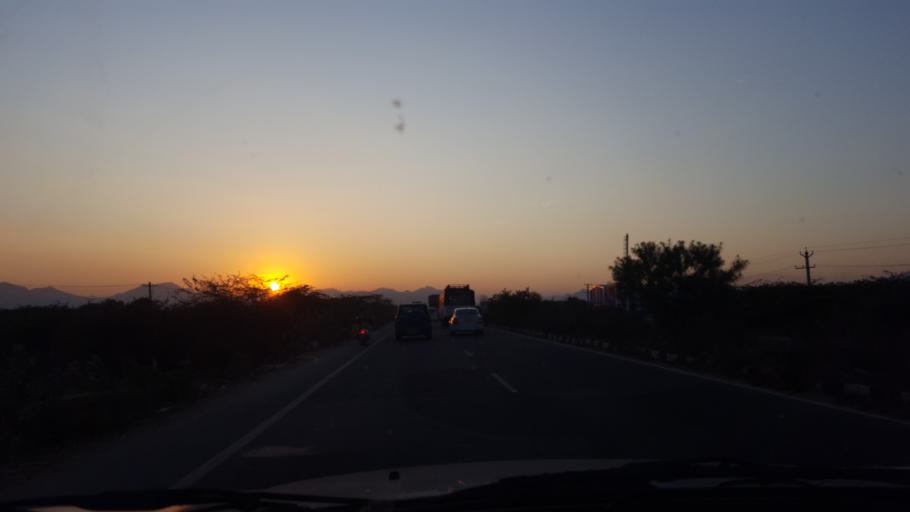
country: IN
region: Andhra Pradesh
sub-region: Chittoor
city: Tirupati
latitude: 13.6043
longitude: 79.3878
